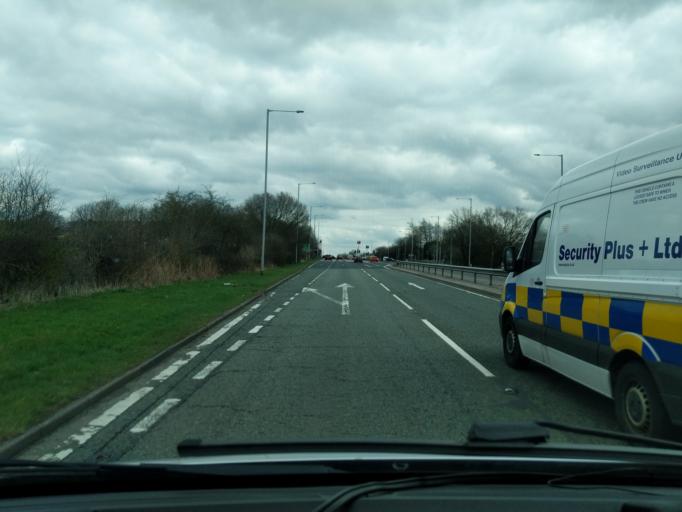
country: GB
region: England
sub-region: St. Helens
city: Haydock
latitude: 53.4726
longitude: -2.6917
